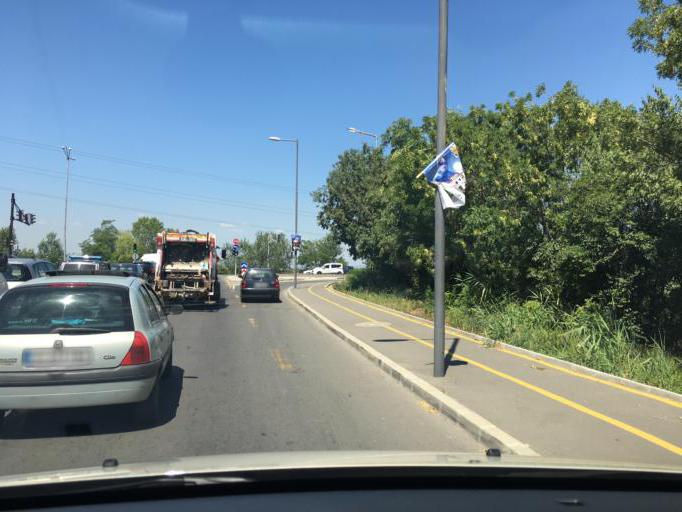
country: BG
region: Burgas
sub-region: Obshtina Burgas
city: Burgas
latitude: 42.4930
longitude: 27.4511
